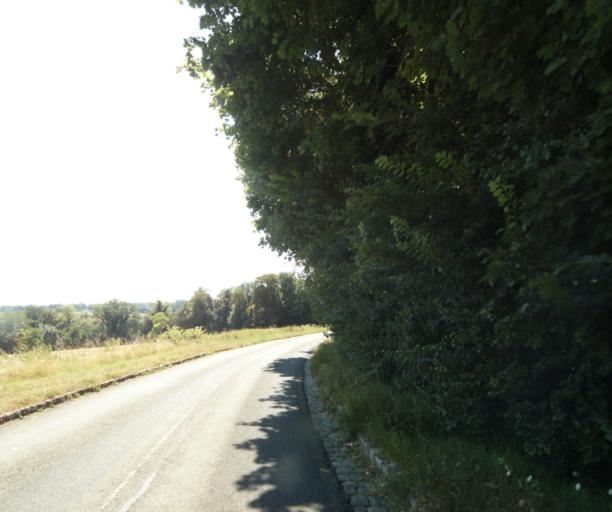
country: FR
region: Ile-de-France
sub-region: Departement de Seine-et-Marne
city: Guermantes
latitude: 48.8638
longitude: 2.7041
